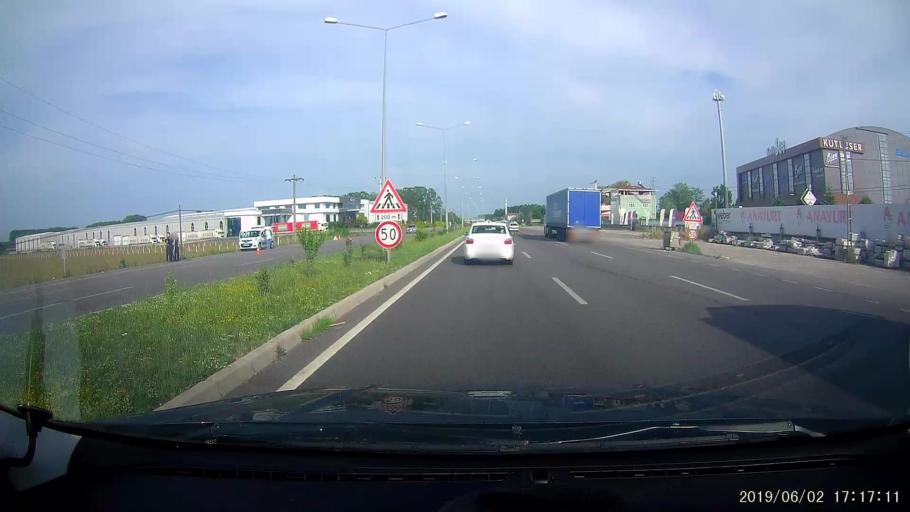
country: TR
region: Samsun
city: Dikbiyik
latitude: 41.2307
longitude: 36.5772
